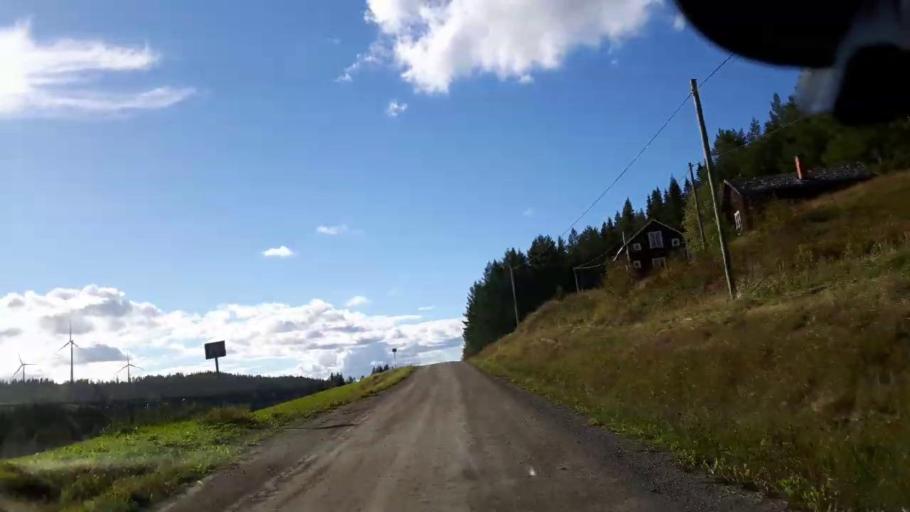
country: SE
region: Jaemtland
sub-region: Ragunda Kommun
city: Hammarstrand
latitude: 63.4761
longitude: 16.1603
